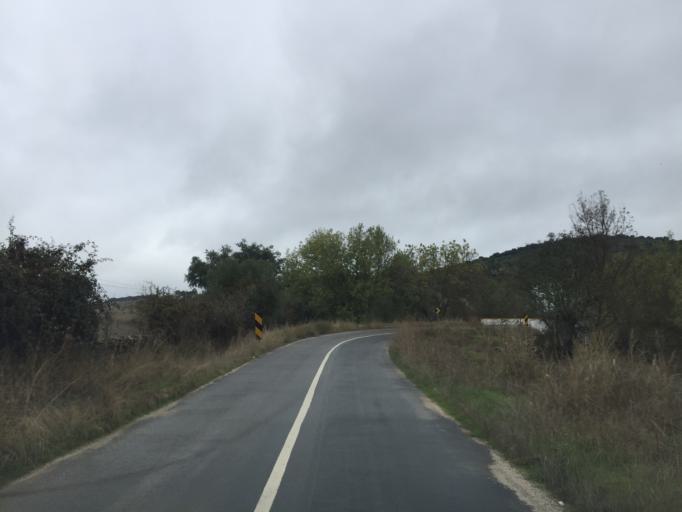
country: PT
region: Portalegre
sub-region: Alter do Chao
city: Alter do Chao
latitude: 39.2263
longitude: -7.6536
